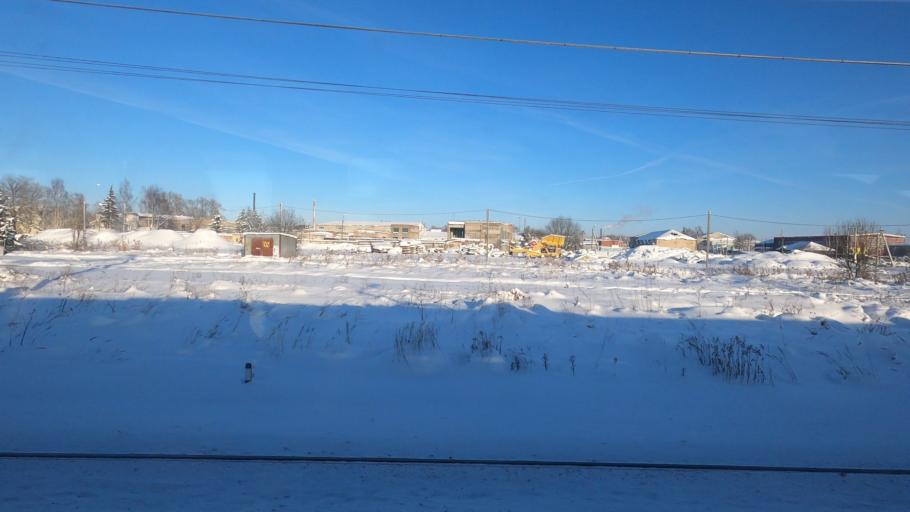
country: RU
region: Moskovskaya
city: Taldom
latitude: 56.7195
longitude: 37.5318
